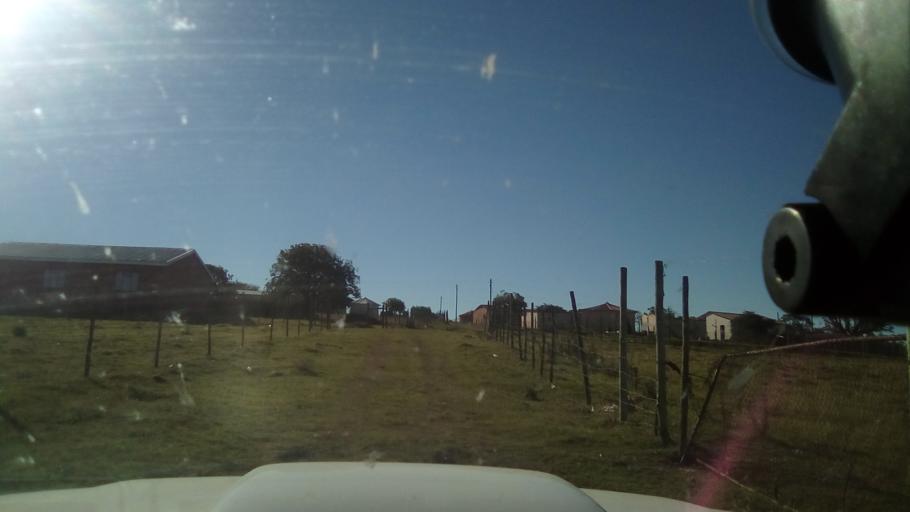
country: ZA
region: Eastern Cape
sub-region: Buffalo City Metropolitan Municipality
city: Bhisho
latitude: -32.9392
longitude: 27.2915
